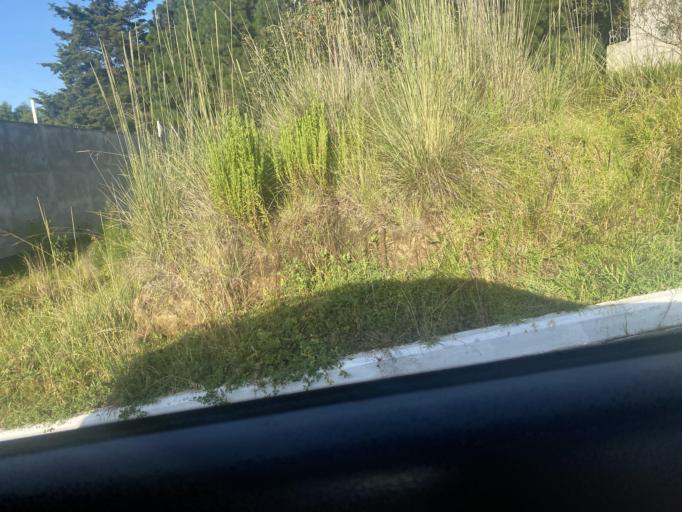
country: GT
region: Quetzaltenango
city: Quetzaltenango
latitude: 14.8538
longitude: -91.5204
